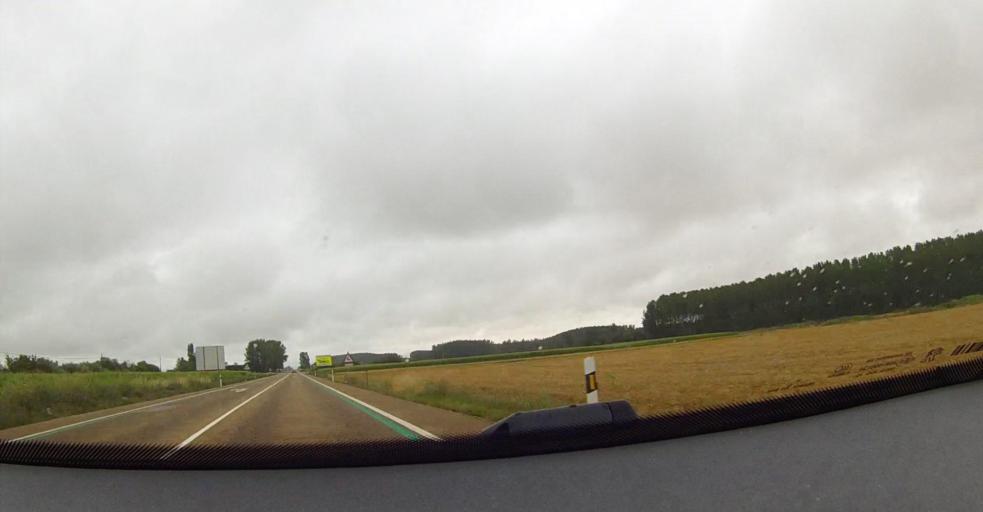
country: ES
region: Castille and Leon
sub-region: Provincia de Palencia
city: Villamoronta
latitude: 42.4115
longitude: -4.6720
